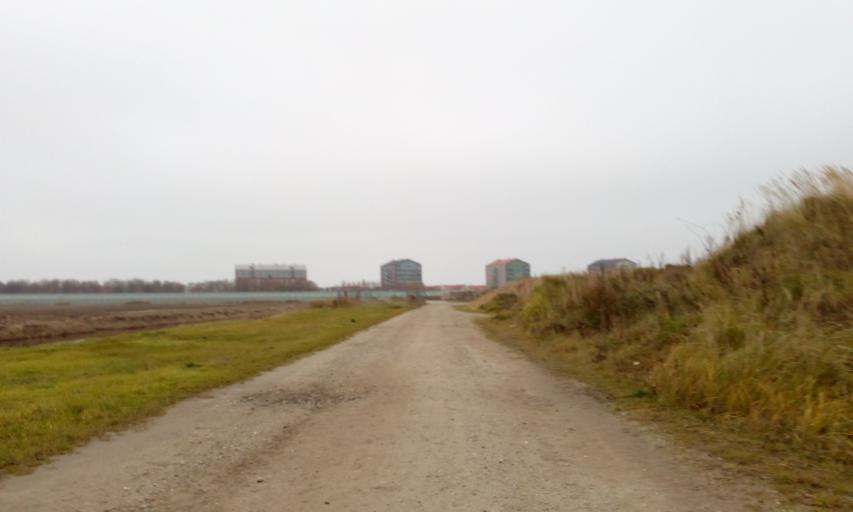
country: NL
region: South Holland
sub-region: Gemeente Lansingerland
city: Berkel en Rodenrijs
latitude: 51.9829
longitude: 4.4805
